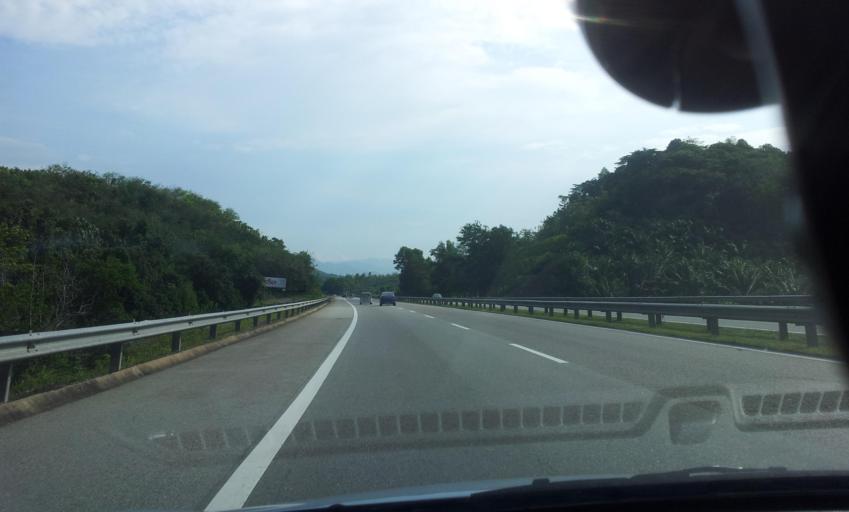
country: MY
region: Pahang
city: Bentong Town
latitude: 3.4905
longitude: 102.0885
